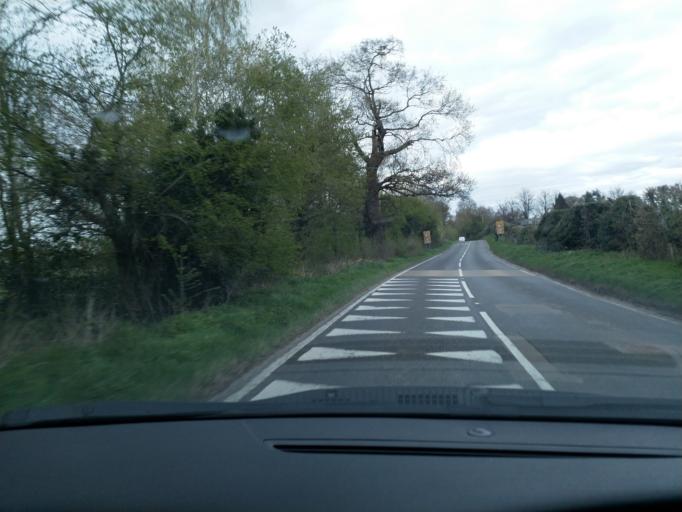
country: GB
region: England
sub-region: Warwickshire
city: Royal Leamington Spa
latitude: 52.2459
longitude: -1.5429
